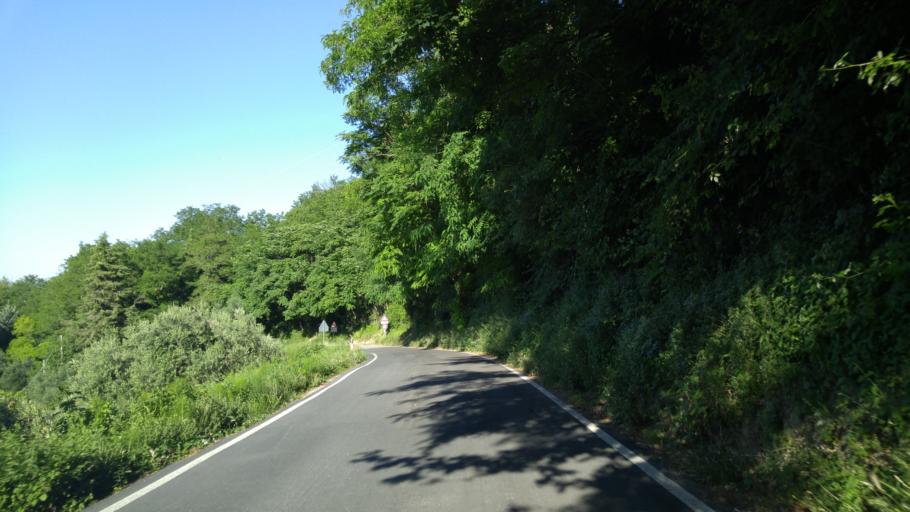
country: IT
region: The Marches
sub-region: Provincia di Pesaro e Urbino
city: Mombaroccio
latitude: 43.7939
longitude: 12.8677
